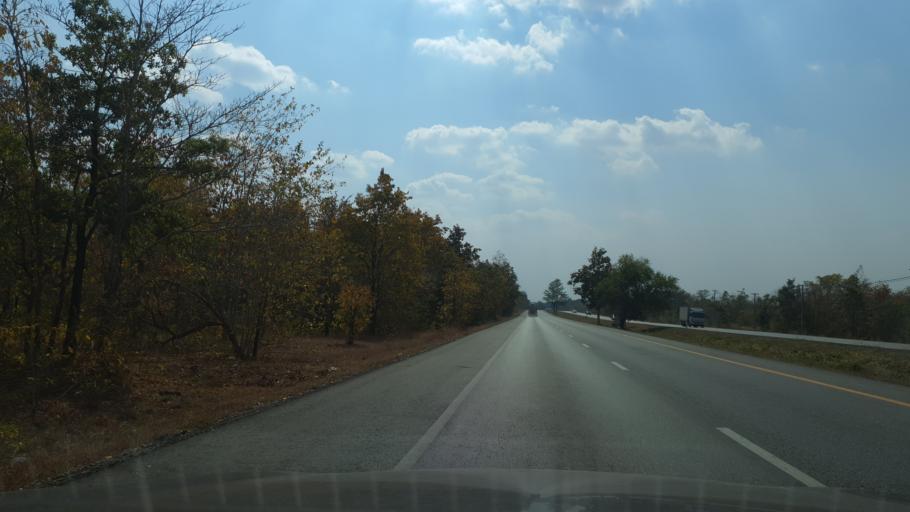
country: TH
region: Lampang
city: Mae Phrik
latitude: 17.3192
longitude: 99.1512
